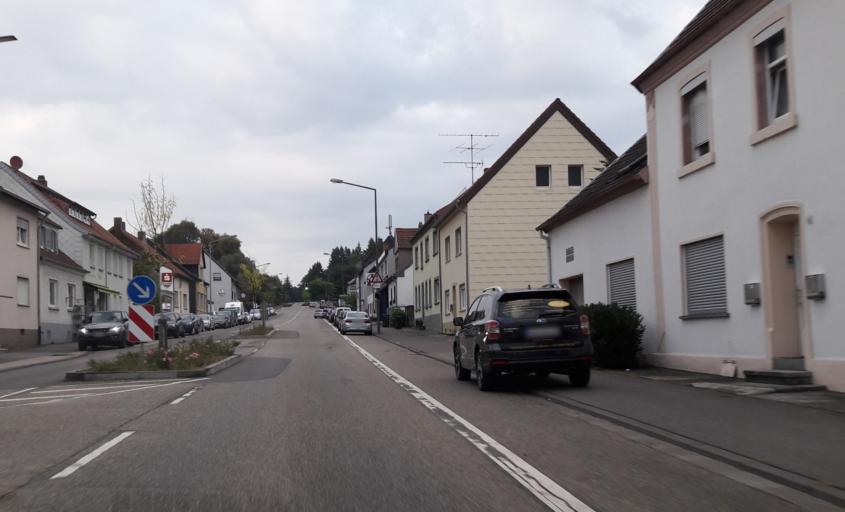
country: DE
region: Saarland
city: Homburg
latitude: 49.2911
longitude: 7.3195
